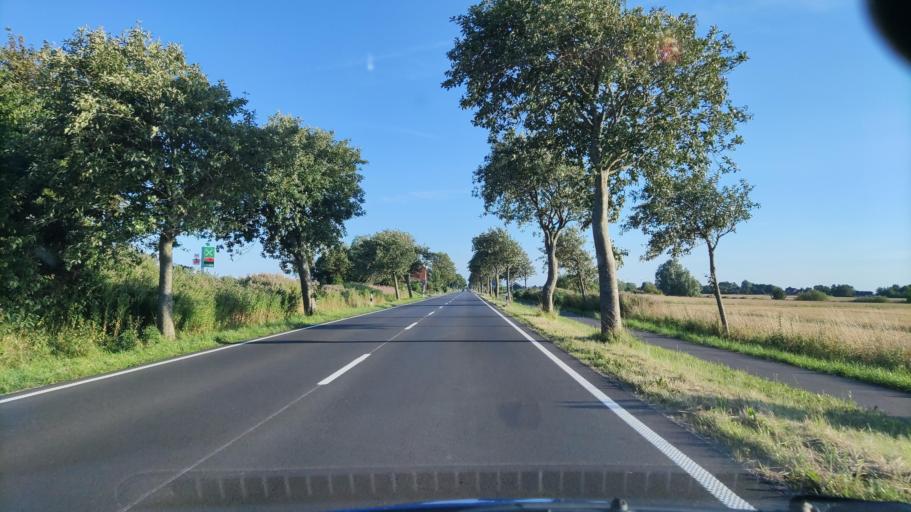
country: DE
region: Lower Saxony
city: Werdum
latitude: 53.6765
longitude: 7.7933
